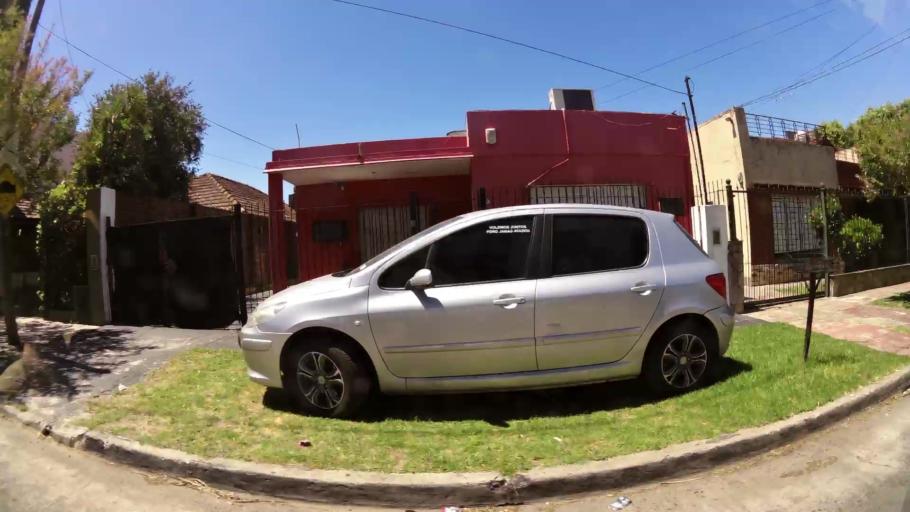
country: AR
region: Buenos Aires
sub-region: Partido de Vicente Lopez
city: Olivos
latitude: -34.5150
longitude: -58.5360
